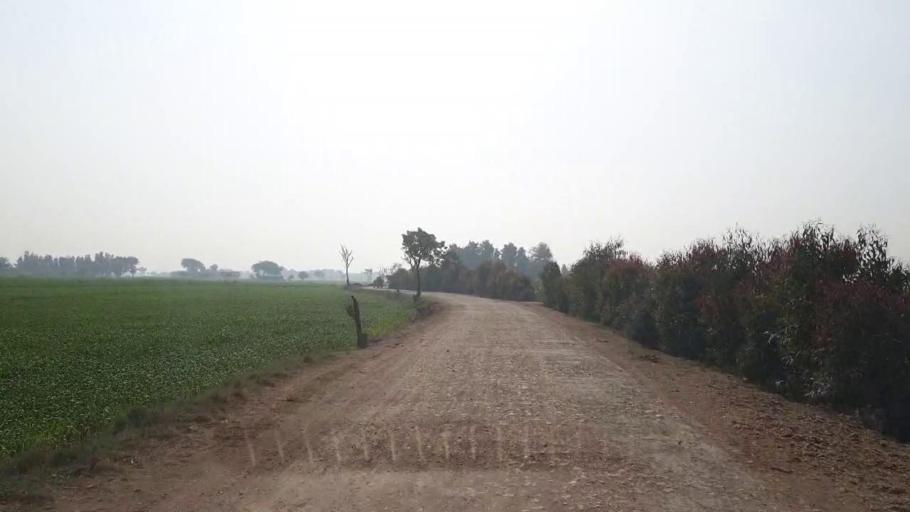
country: PK
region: Sindh
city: Bhit Shah
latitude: 25.7365
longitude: 68.5190
